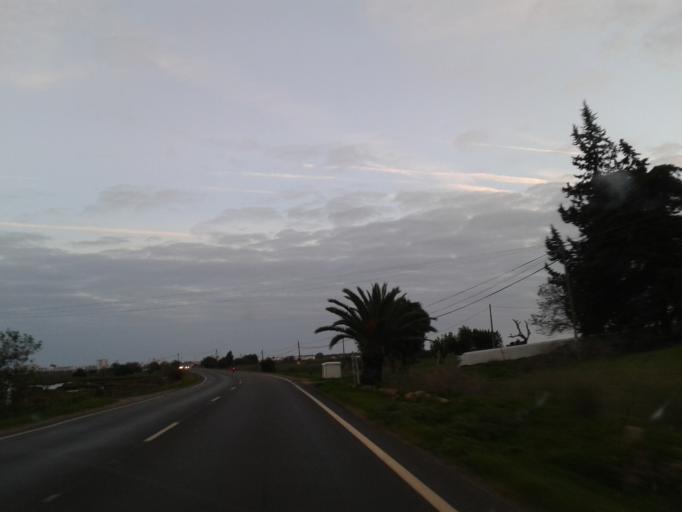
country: PT
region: Faro
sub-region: Castro Marim
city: Castro Marim
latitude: 37.2099
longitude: -7.4371
